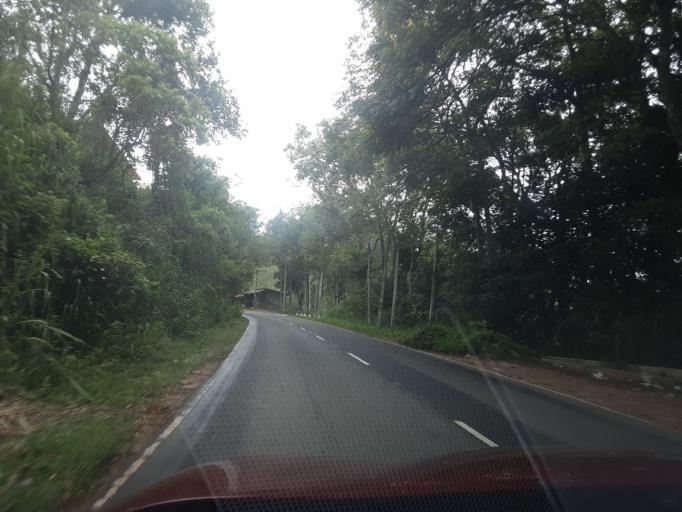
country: LK
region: Uva
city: Haputale
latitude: 6.8559
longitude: 80.9677
